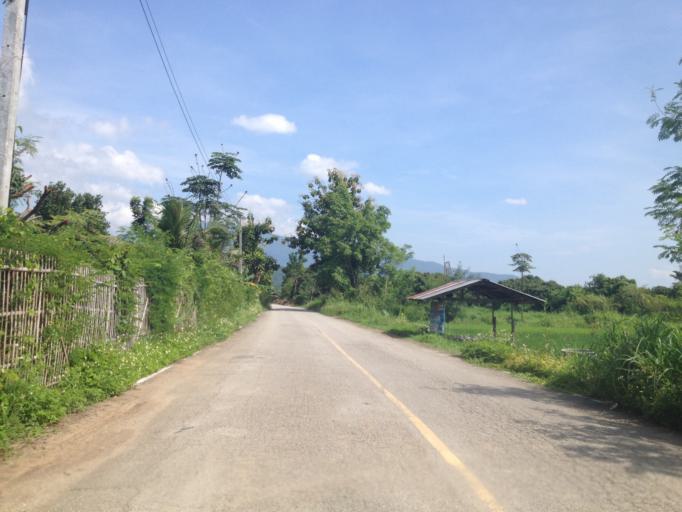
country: TH
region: Chiang Mai
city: Hang Dong
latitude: 18.7196
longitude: 98.9078
